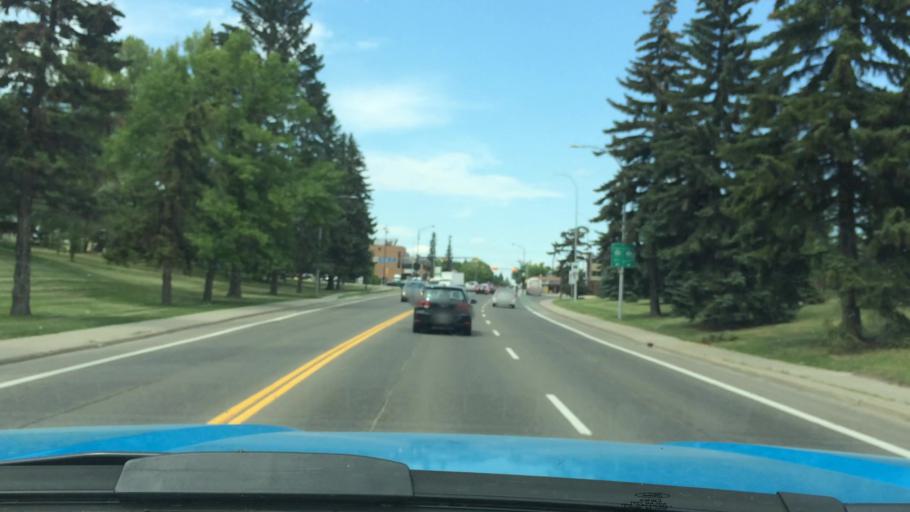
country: CA
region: Alberta
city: Calgary
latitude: 51.0652
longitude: -114.0848
